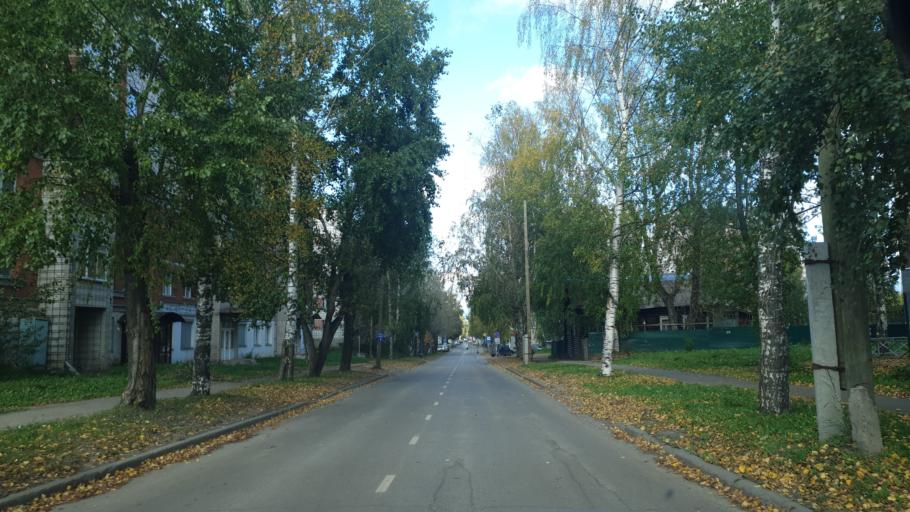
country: RU
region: Komi Republic
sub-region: Syktyvdinskiy Rayon
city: Syktyvkar
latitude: 61.6624
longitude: 50.8425
